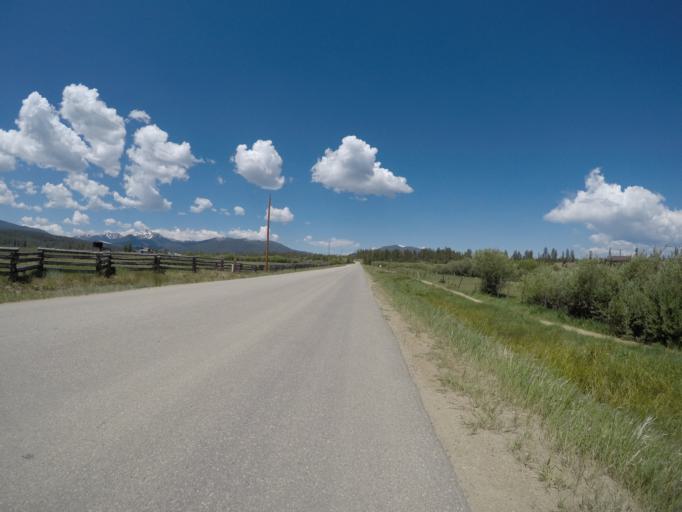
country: US
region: Colorado
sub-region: Grand County
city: Fraser
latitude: 39.9447
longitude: -105.8248
